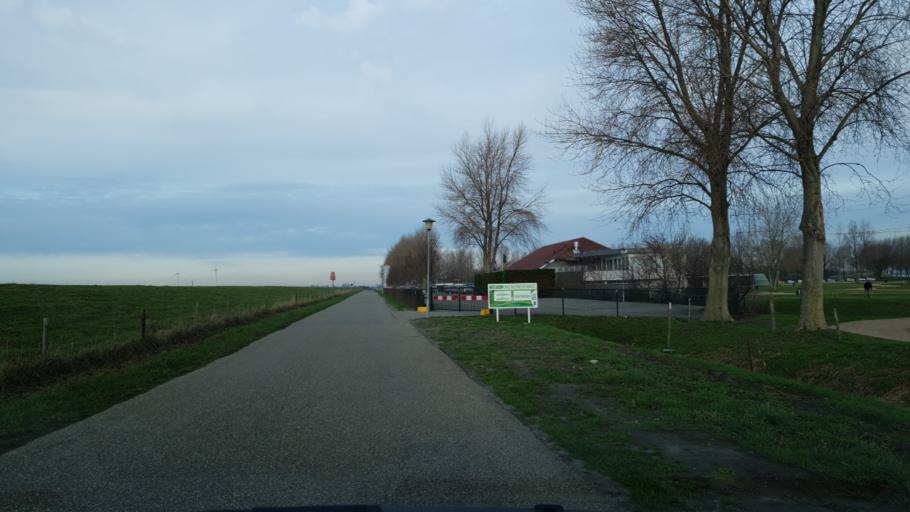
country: NL
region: North Brabant
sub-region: Gemeente Woensdrecht
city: Woensdrecht
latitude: 51.3889
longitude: 4.2395
